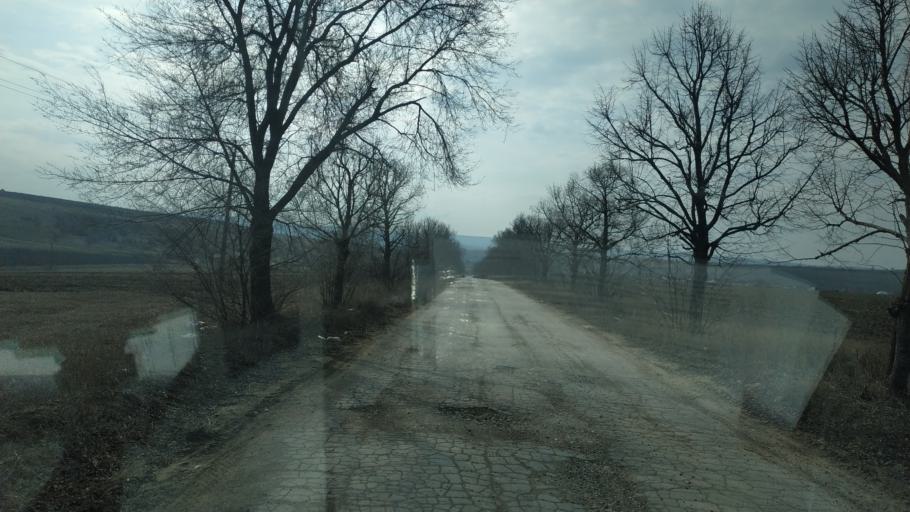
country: MD
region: Anenii Noi
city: Anenii Noi
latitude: 46.9388
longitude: 29.1088
